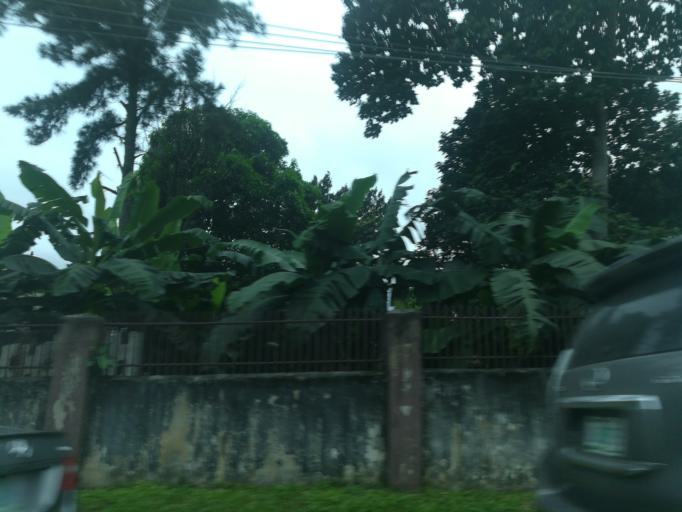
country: NG
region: Rivers
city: Port Harcourt
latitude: 4.8157
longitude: 7.0011
